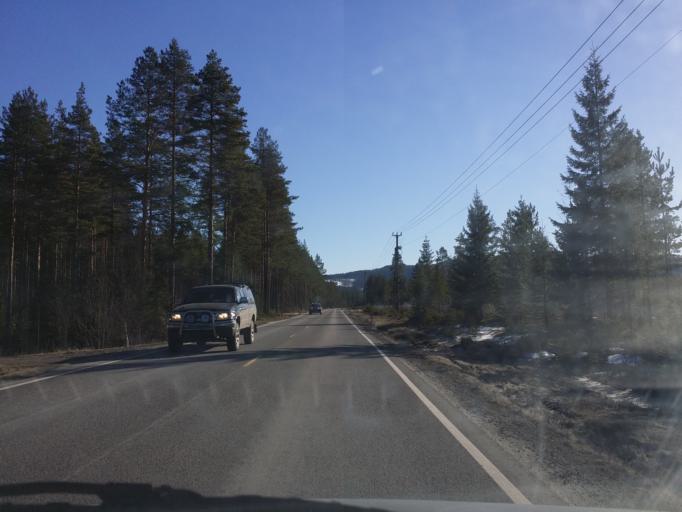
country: NO
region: Buskerud
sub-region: Ringerike
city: Honefoss
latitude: 60.3446
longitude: 10.1066
